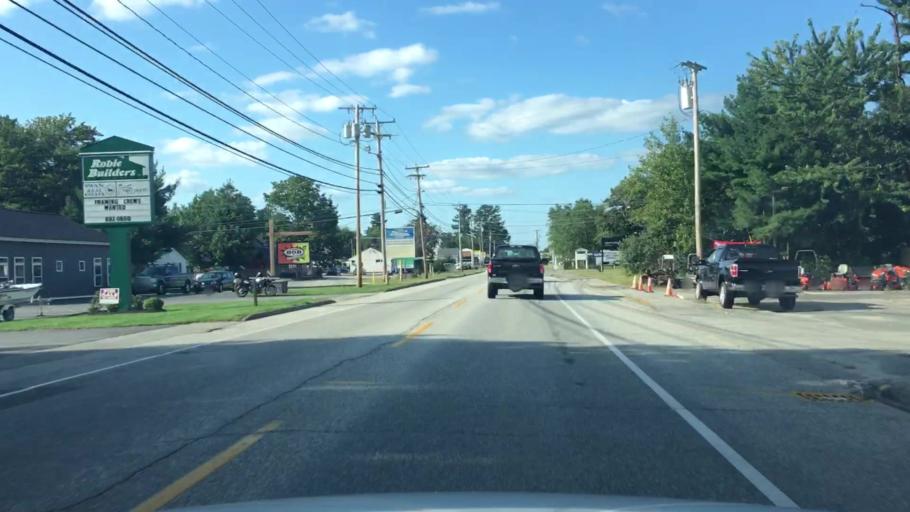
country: US
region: Maine
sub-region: Cumberland County
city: North Windham
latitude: 43.8227
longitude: -70.4342
